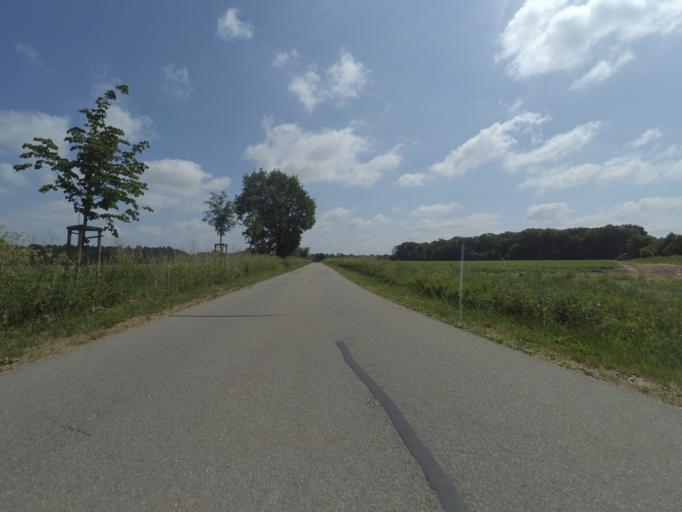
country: DE
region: Mecklenburg-Vorpommern
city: Siggelkow
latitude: 53.4149
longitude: 11.9735
